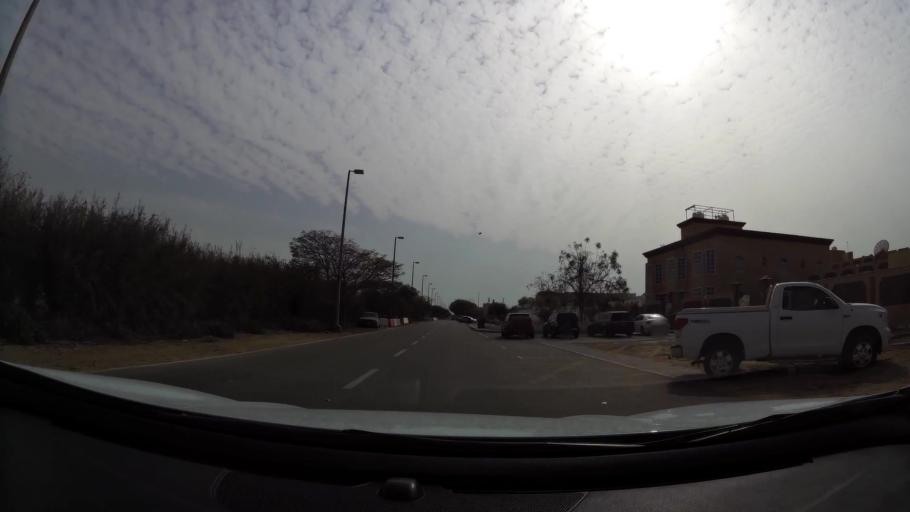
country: AE
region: Abu Dhabi
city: Abu Dhabi
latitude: 24.6022
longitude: 54.7048
